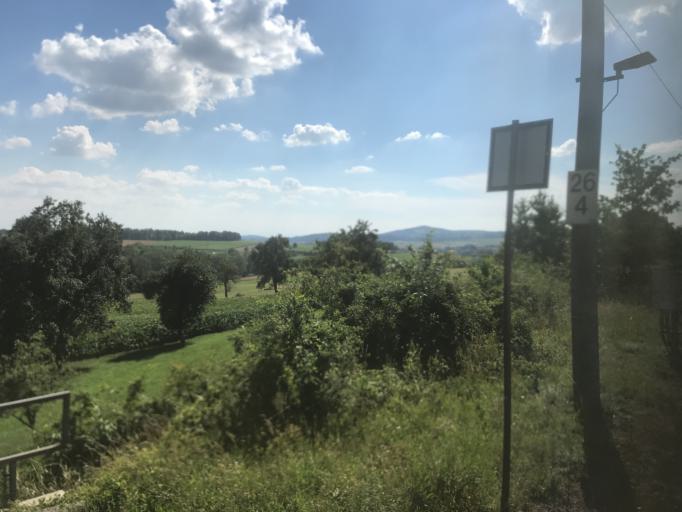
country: AT
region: Upper Austria
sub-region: Politischer Bezirk Urfahr-Umgebung
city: Engerwitzdorf
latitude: 48.3297
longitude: 14.5117
